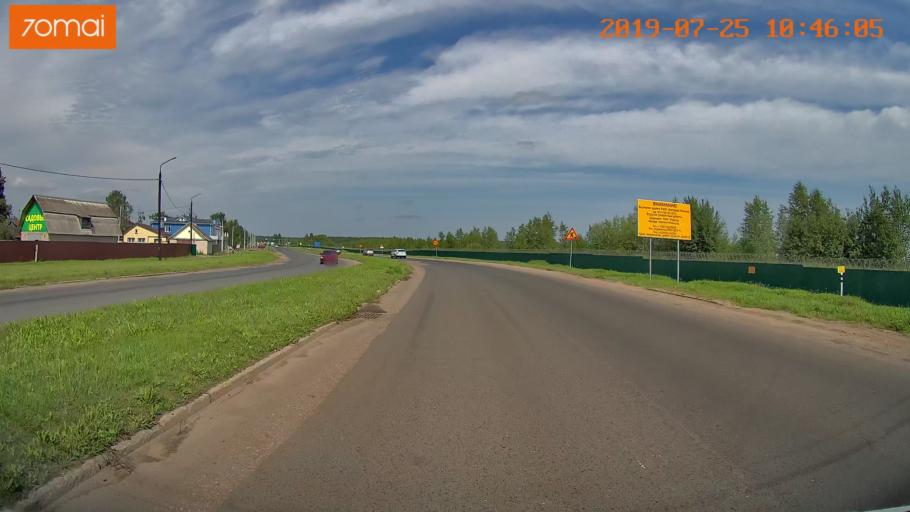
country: RU
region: Ivanovo
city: Bogorodskoye
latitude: 57.0565
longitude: 40.9634
